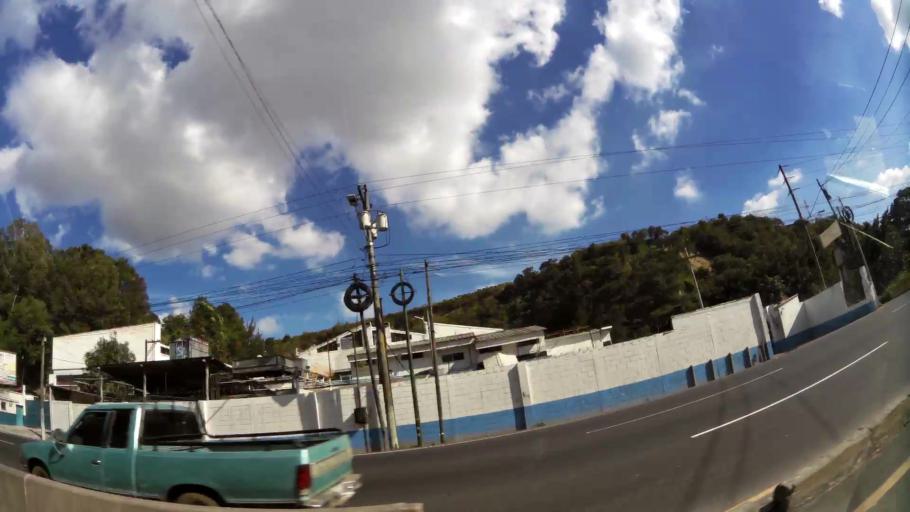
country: GT
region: Guatemala
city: Villa Nueva
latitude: 14.5547
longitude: -90.5768
